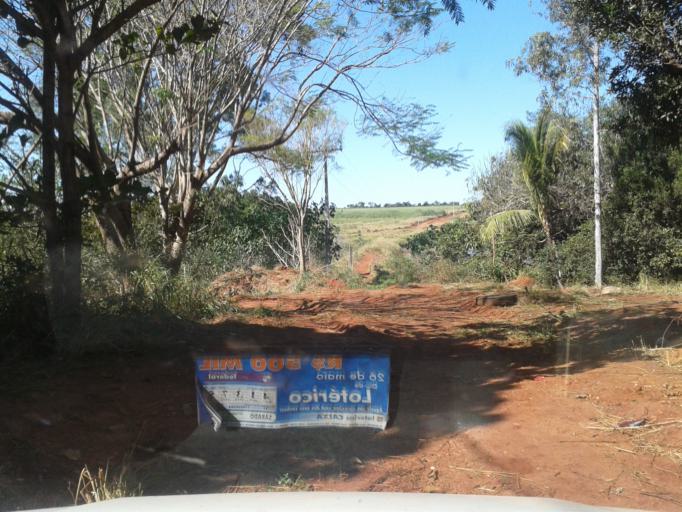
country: BR
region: Minas Gerais
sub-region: Santa Vitoria
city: Santa Vitoria
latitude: -19.0598
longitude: -50.3830
